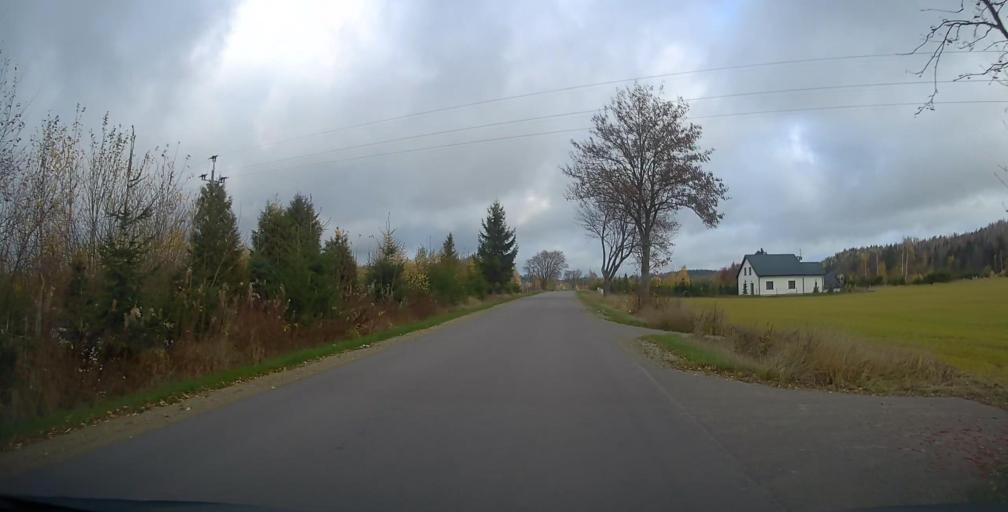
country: PL
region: Podlasie
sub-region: Suwalki
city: Suwalki
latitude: 54.2937
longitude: 22.8786
